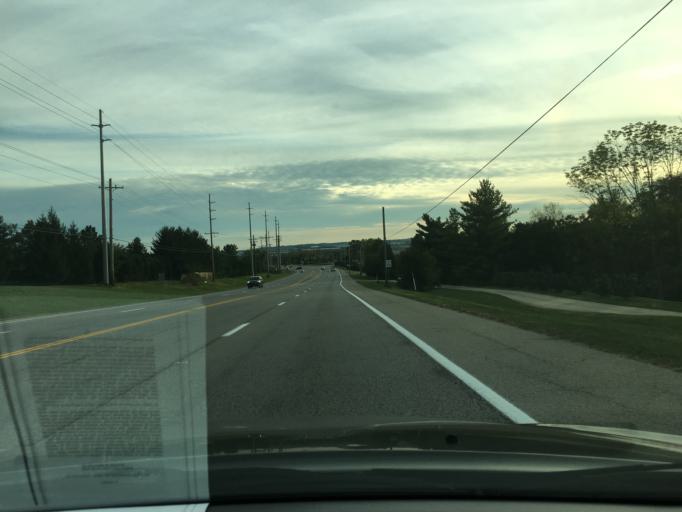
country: US
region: Ohio
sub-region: Butler County
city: Beckett Ridge
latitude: 39.3657
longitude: -84.4584
